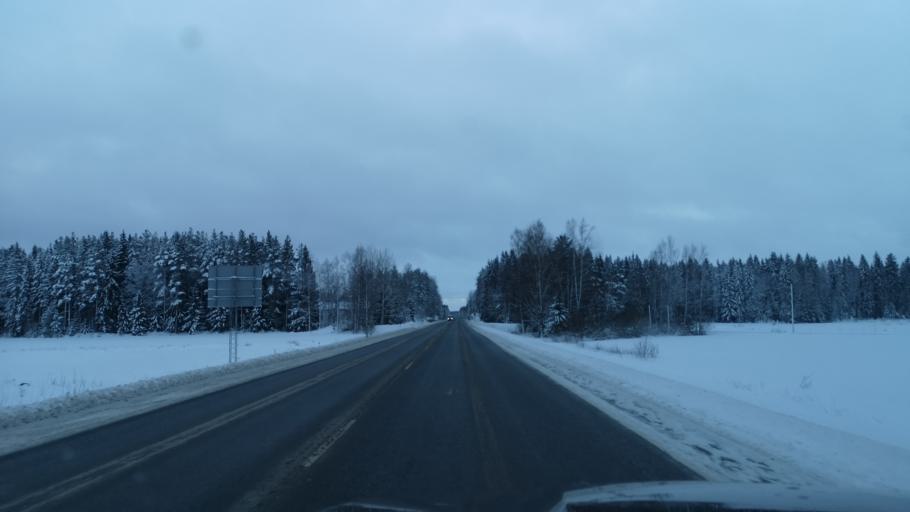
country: FI
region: Varsinais-Suomi
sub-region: Loimaa
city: Loimaa
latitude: 60.9158
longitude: 23.1884
